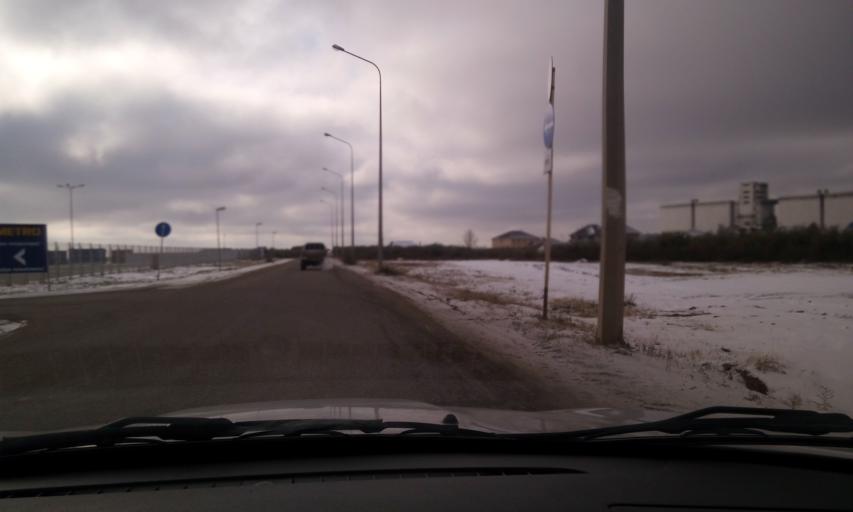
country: KZ
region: Astana Qalasy
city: Astana
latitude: 51.1324
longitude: 71.5438
